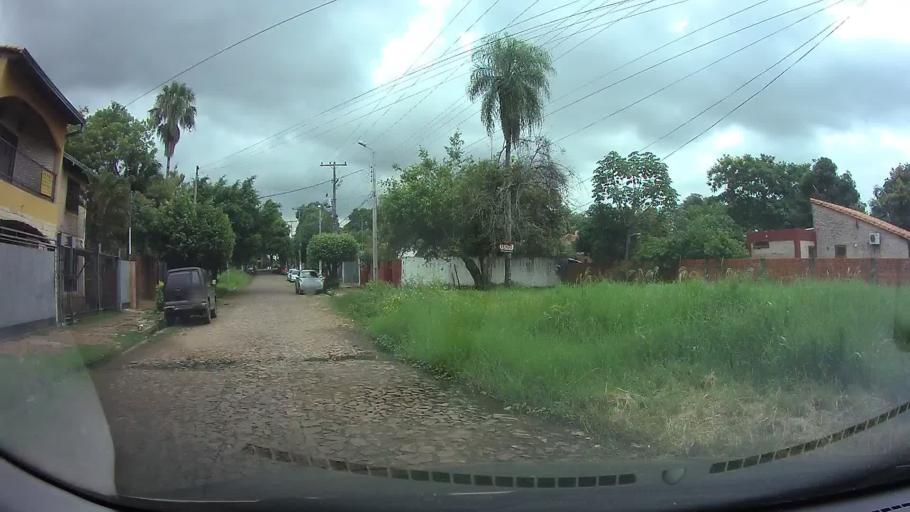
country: PY
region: Central
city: San Lorenzo
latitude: -25.2642
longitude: -57.4782
